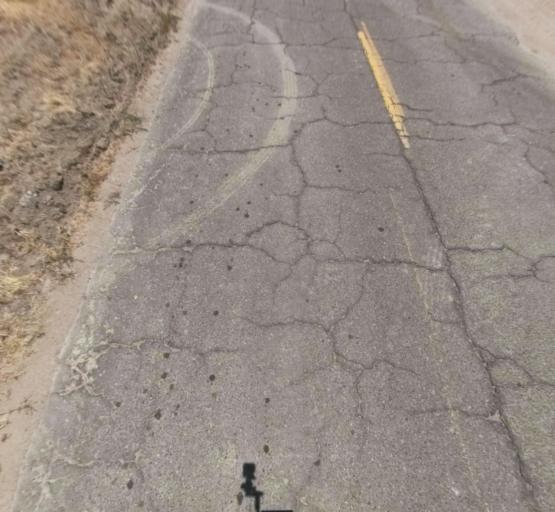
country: US
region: California
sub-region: Fresno County
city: Biola
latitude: 36.8491
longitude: -120.0921
